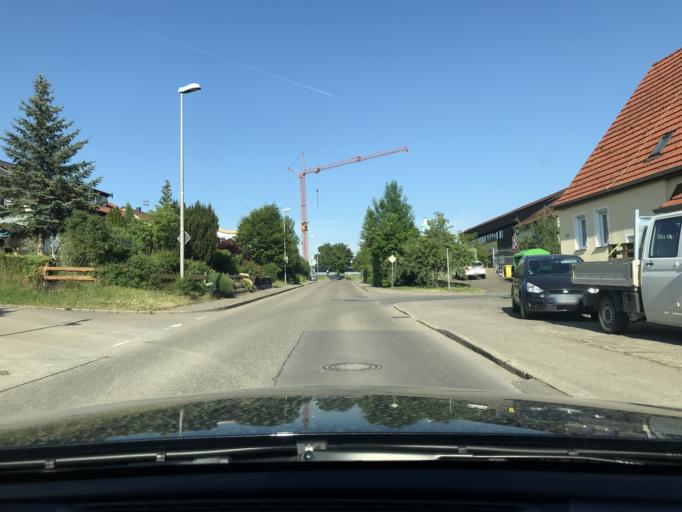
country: DE
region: Baden-Wuerttemberg
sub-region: Regierungsbezirk Stuttgart
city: Schwaikheim
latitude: 48.8907
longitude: 9.3216
